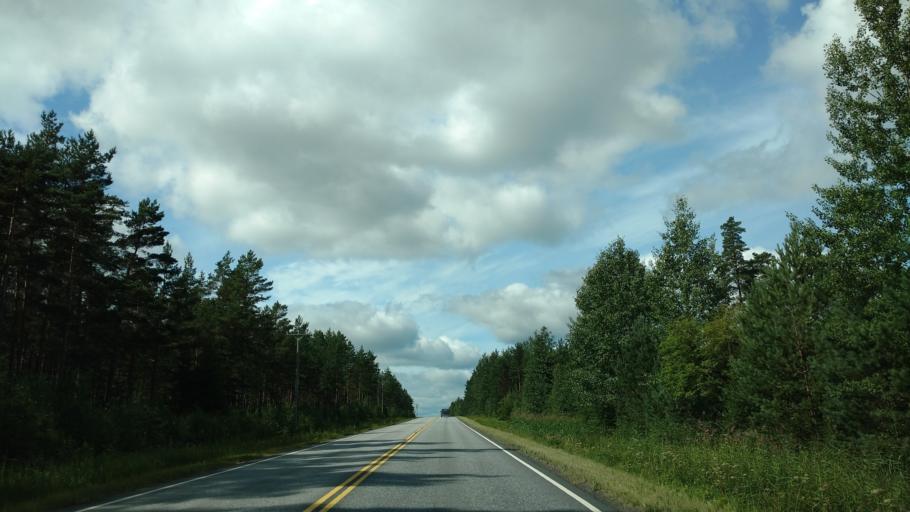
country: FI
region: Varsinais-Suomi
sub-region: Salo
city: Pernioe
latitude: 60.2018
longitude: 23.0909
